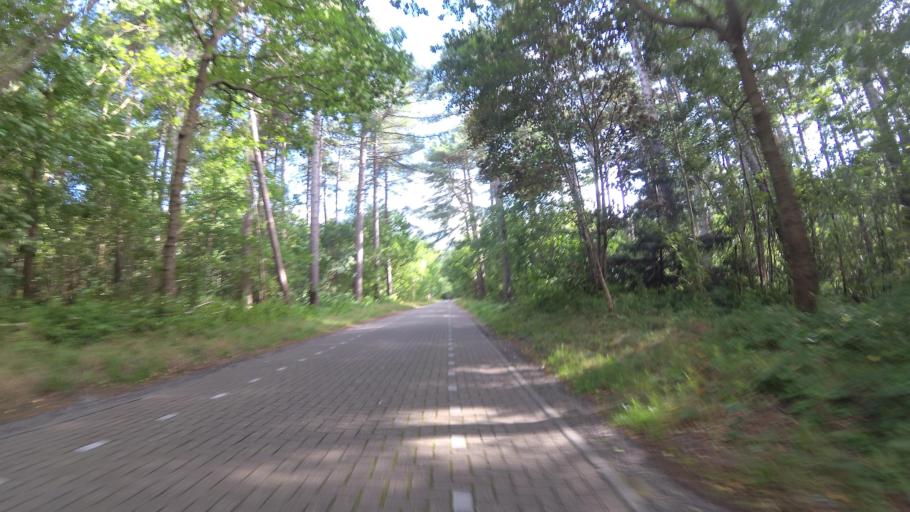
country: NL
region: North Holland
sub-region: Gemeente Texel
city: Den Burg
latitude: 53.0682
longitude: 4.7508
